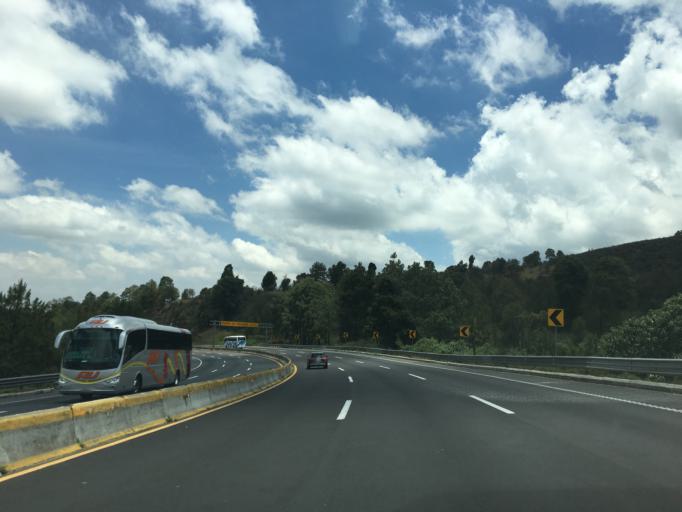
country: MX
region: Mexico
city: Rio Frio de Juarez
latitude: 19.3034
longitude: -98.7494
